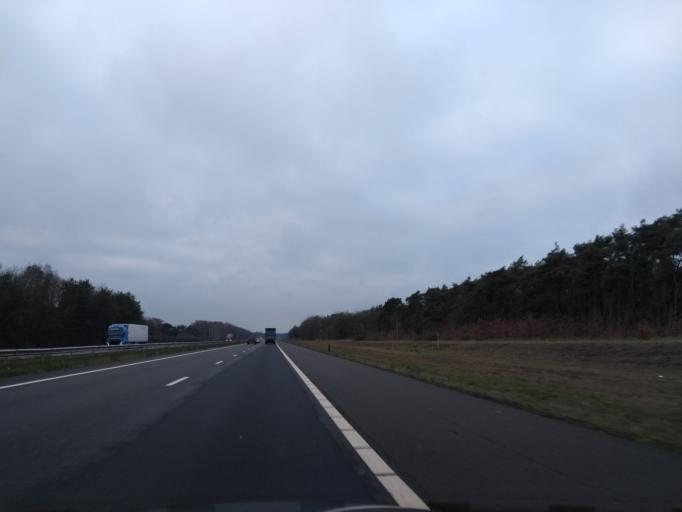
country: NL
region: Overijssel
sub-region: Gemeente Hof van Twente
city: Markelo
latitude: 52.2819
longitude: 6.5106
